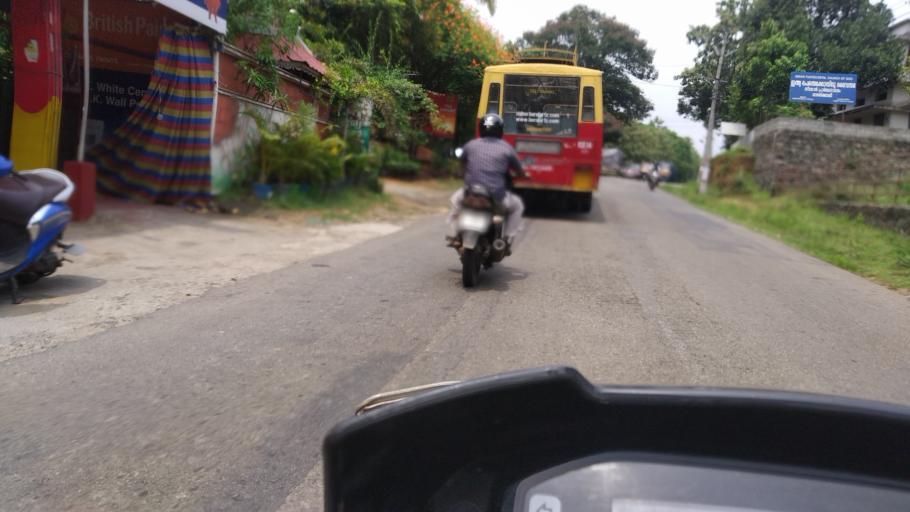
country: IN
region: Kerala
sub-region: Ernakulam
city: Perumpavur
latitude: 10.0963
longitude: 76.5523
